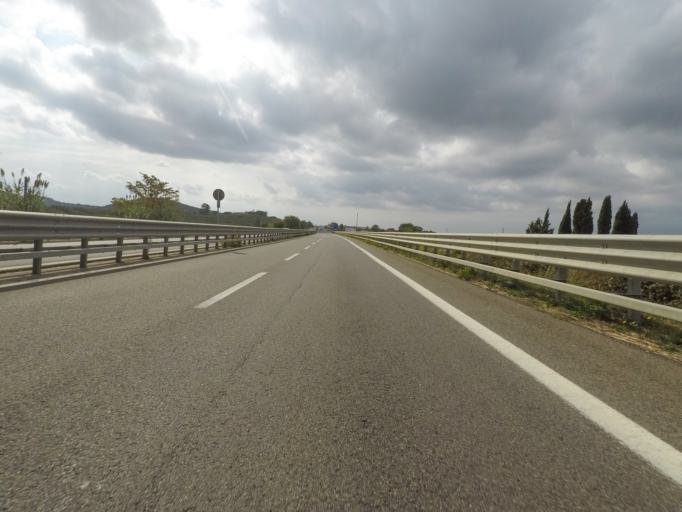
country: IT
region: Tuscany
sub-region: Provincia di Grosseto
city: Bagno Roselle
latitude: 42.8305
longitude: 11.1412
